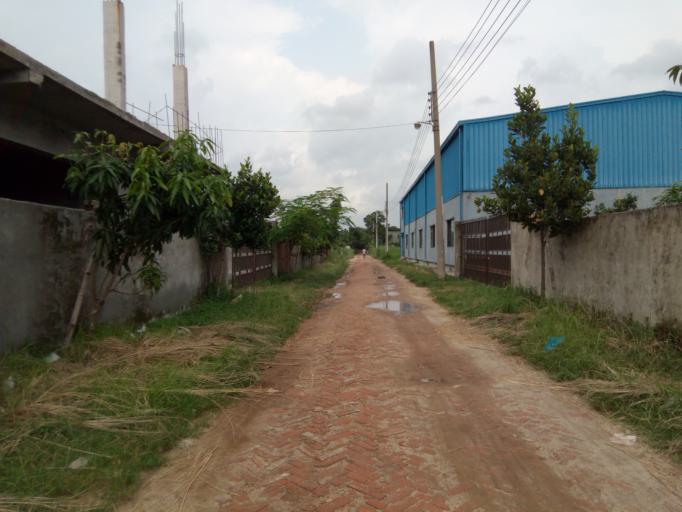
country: BD
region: Dhaka
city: Azimpur
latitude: 23.7532
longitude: 90.3397
